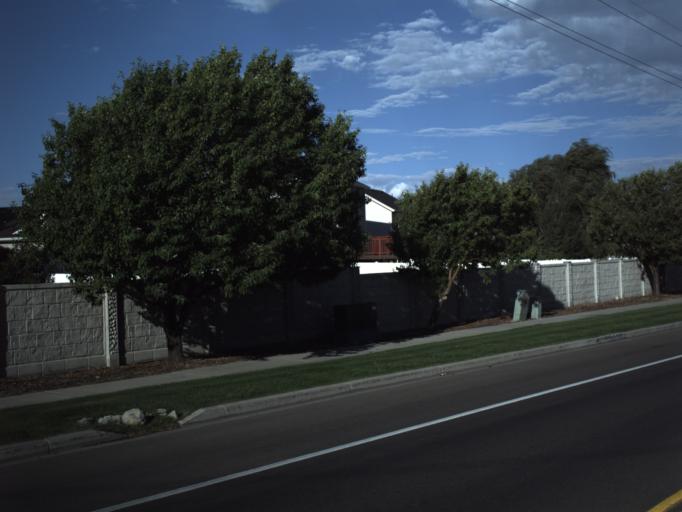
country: US
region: Utah
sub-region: Utah County
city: Spanish Fork
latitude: 40.0956
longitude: -111.6144
